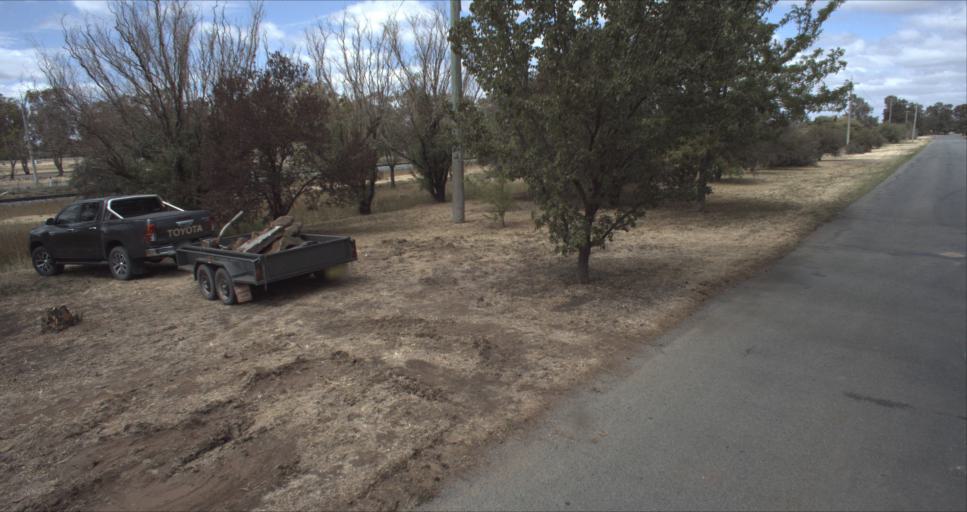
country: AU
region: New South Wales
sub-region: Leeton
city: Leeton
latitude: -34.5619
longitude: 146.3996
